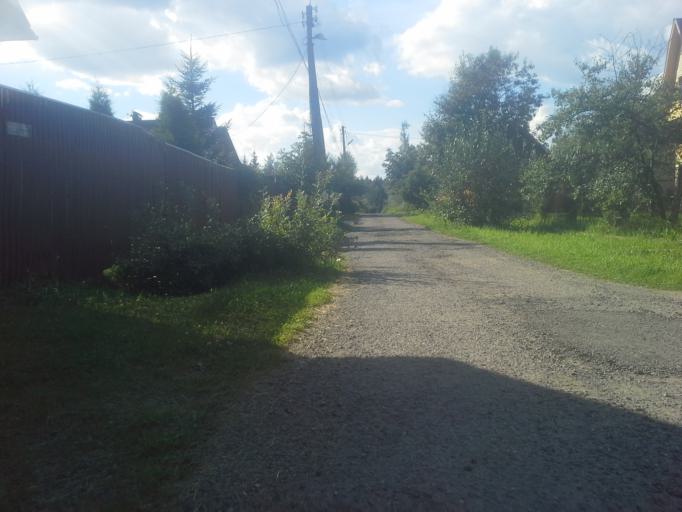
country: RU
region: Moskovskaya
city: Kievskij
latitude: 55.3416
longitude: 36.9557
